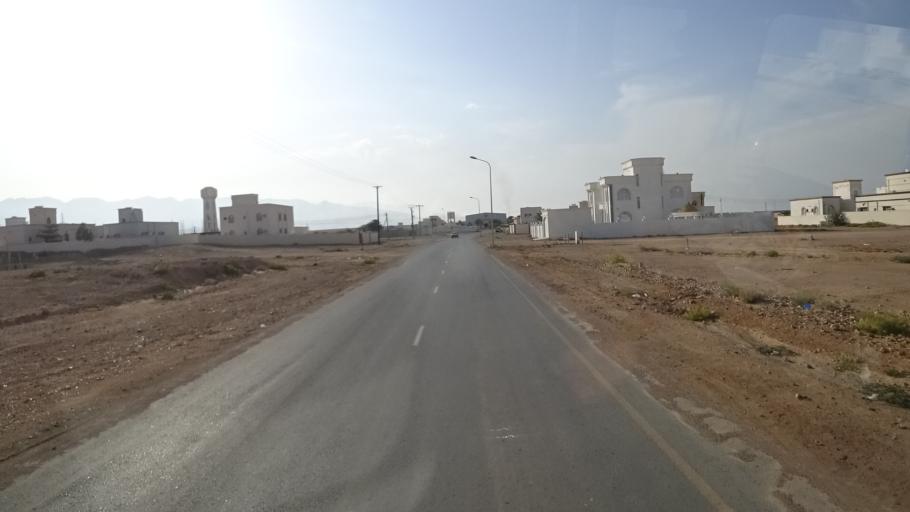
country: OM
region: Ash Sharqiyah
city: Sur
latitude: 22.6190
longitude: 59.4580
